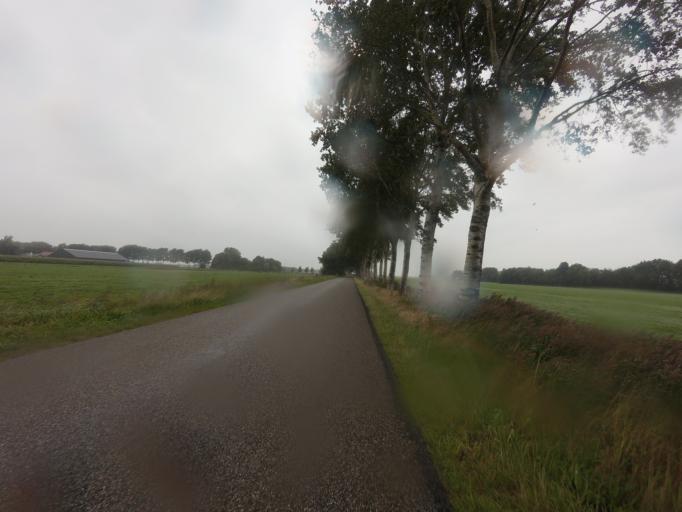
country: NL
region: Friesland
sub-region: Gemeente Opsterland
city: Tijnje
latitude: 53.0176
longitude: 5.9521
